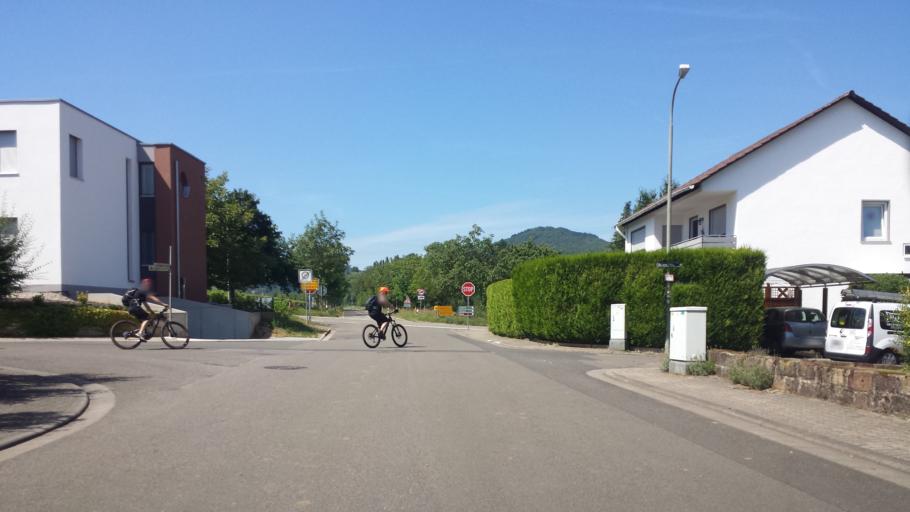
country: DE
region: Rheinland-Pfalz
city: Ilbesheim
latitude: 49.1847
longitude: 8.0493
